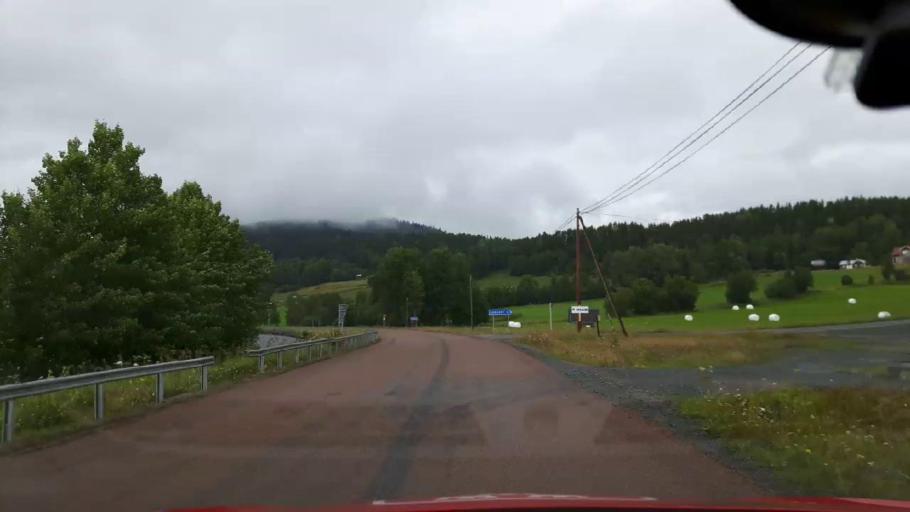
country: SE
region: Jaemtland
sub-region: Krokoms Kommun
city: Valla
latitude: 63.3781
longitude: 14.0156
